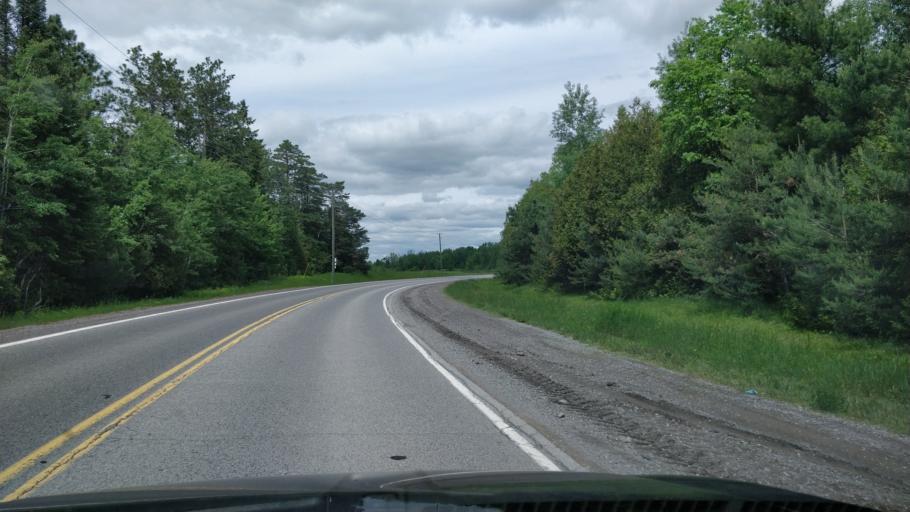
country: CA
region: Ontario
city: Carleton Place
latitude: 45.1089
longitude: -75.9729
